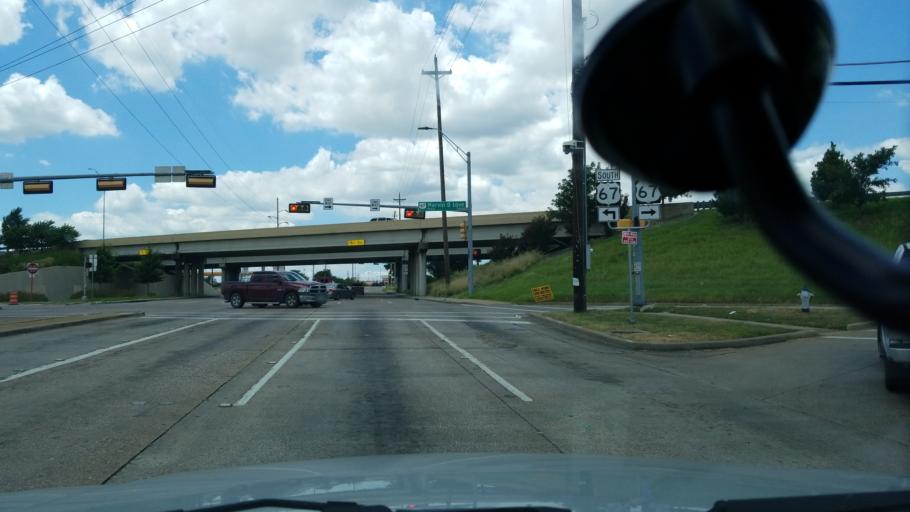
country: US
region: Texas
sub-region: Dallas County
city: Duncanville
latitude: 32.6622
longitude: -96.8689
